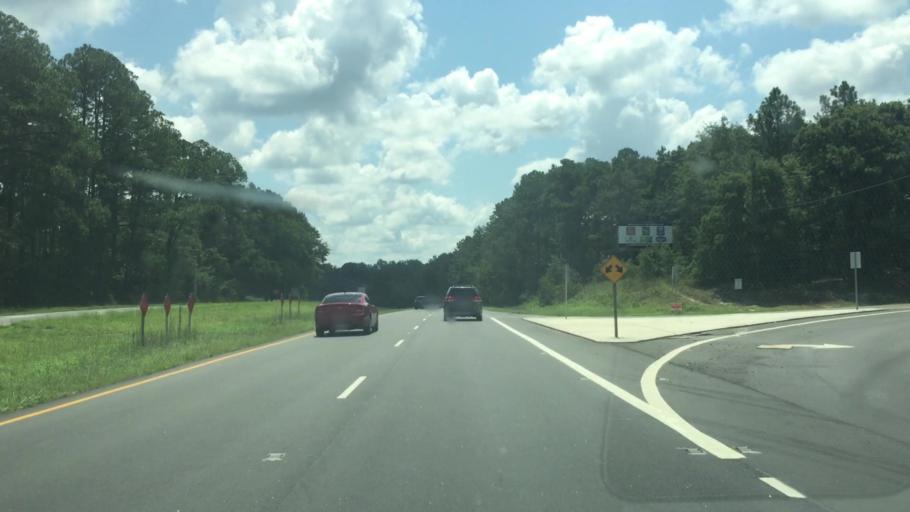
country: US
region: North Carolina
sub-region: Scotland County
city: Laurel Hill
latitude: 34.8019
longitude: -79.5376
